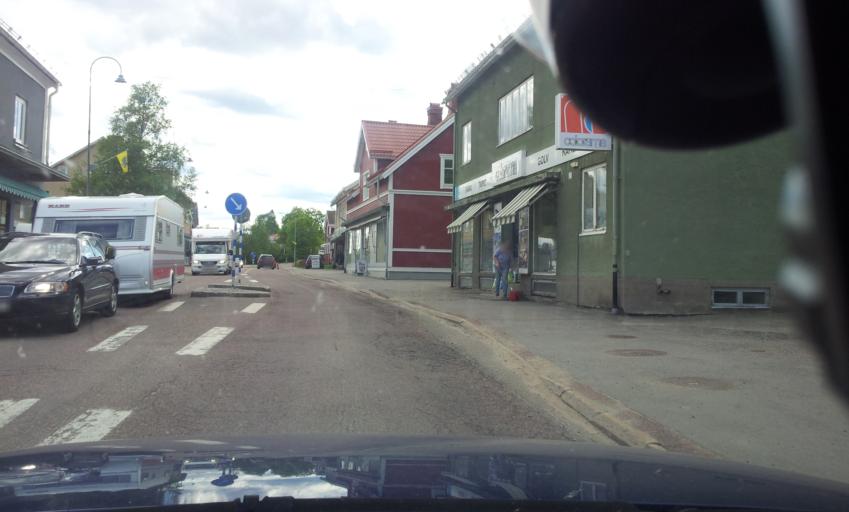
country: SE
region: Gaevleborg
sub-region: Ljusdals Kommun
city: Jaervsoe
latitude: 61.7149
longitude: 16.1694
